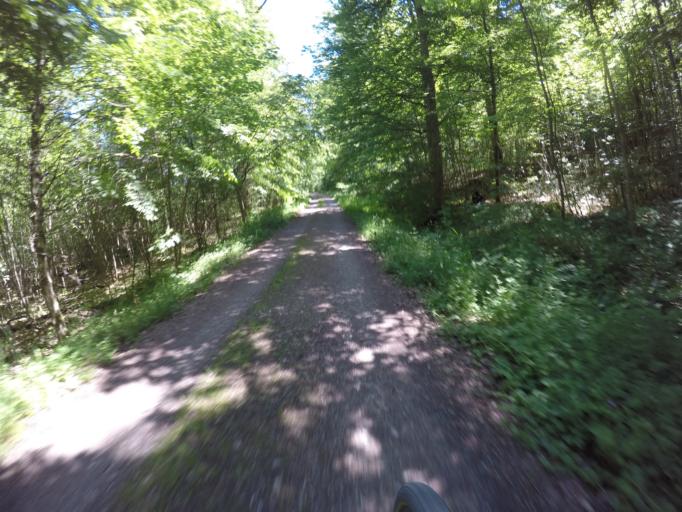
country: DE
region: Baden-Wuerttemberg
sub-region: Regierungsbezirk Stuttgart
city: Gerlingen
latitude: 48.7439
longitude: 9.0812
